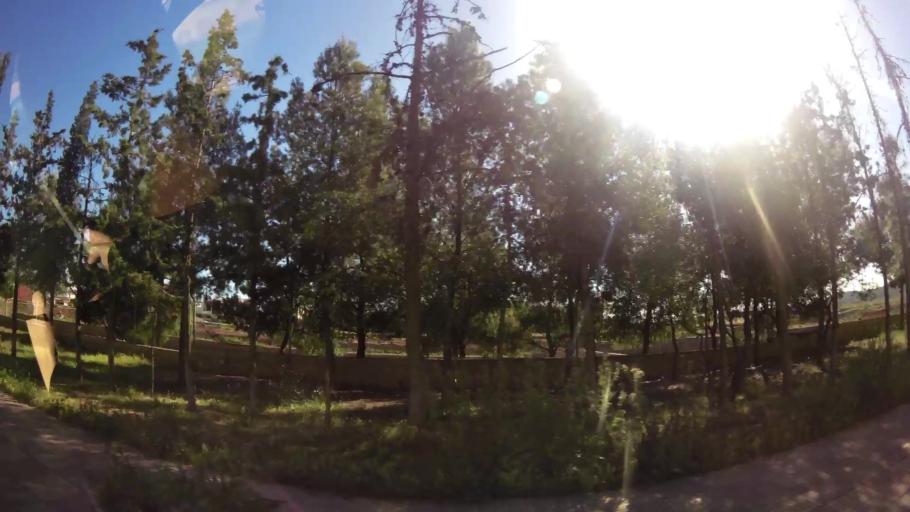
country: MA
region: Oriental
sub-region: Oujda-Angad
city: Oujda
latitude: 34.6512
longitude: -1.8925
